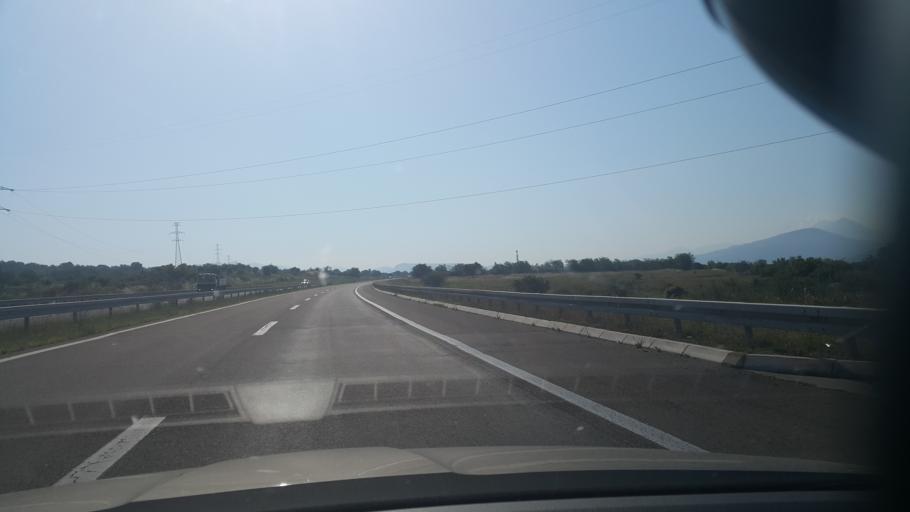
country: RS
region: Central Serbia
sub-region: Nisavski Okrug
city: Nis
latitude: 43.3424
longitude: 21.8972
